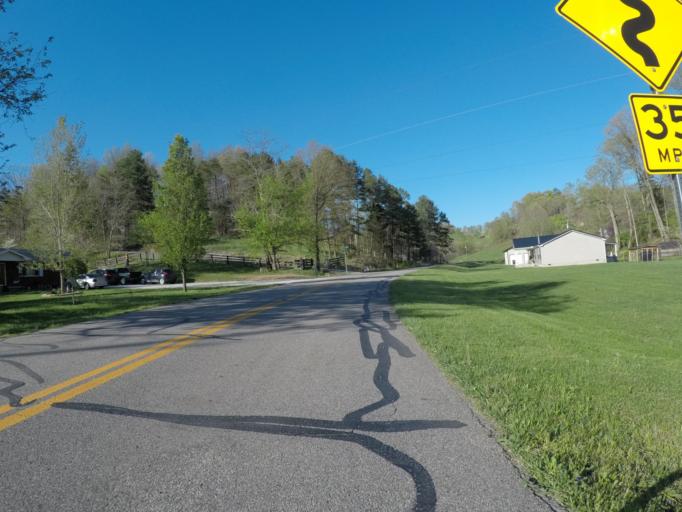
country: US
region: Kentucky
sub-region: Boyd County
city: Meads
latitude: 38.3680
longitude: -82.6637
